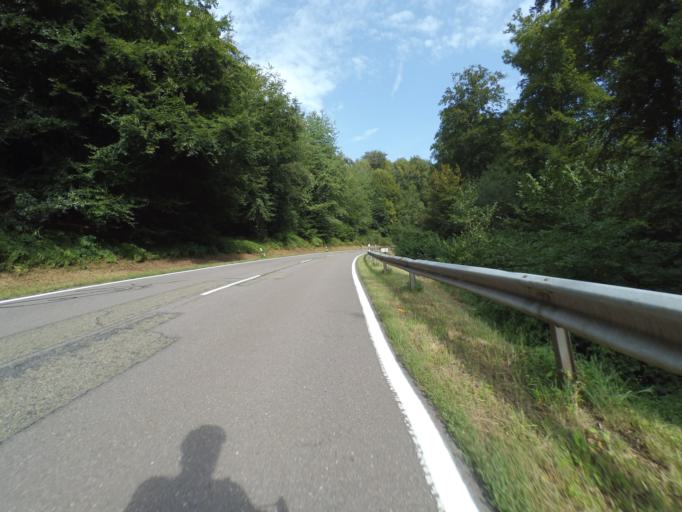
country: DE
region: Rheinland-Pfalz
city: Mannebach
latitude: 49.6335
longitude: 6.5255
